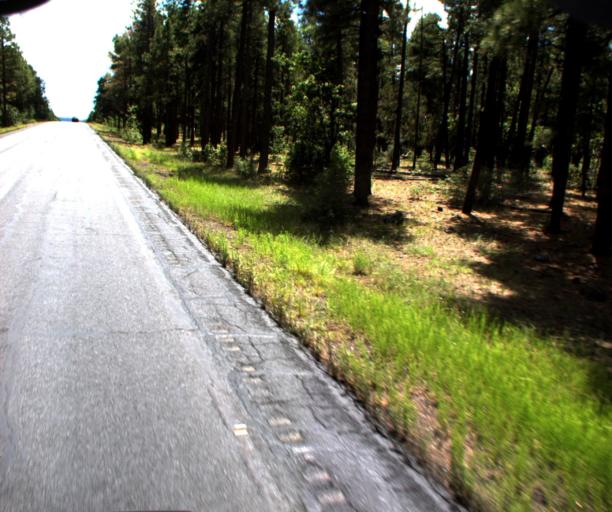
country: US
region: Arizona
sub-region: Gila County
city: Pine
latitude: 34.4892
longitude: -111.4566
